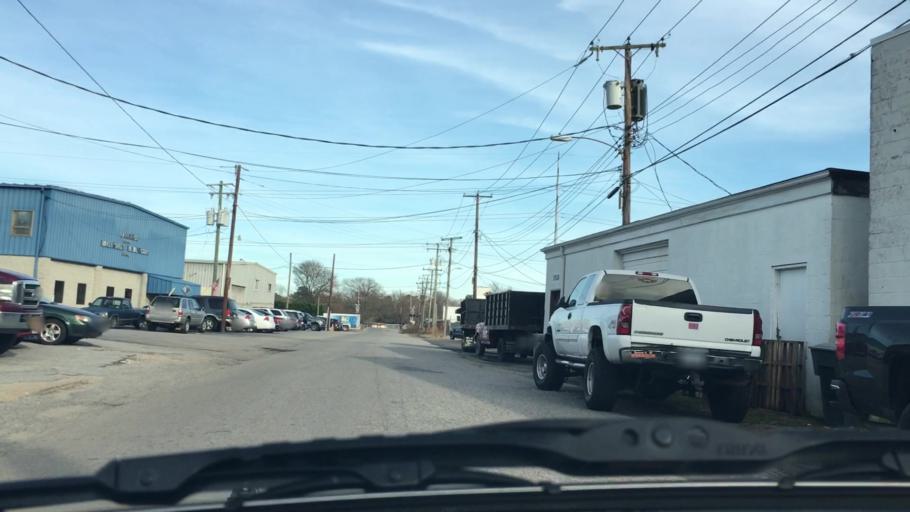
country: US
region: Virginia
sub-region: City of Norfolk
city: Norfolk
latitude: 36.8820
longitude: -76.2546
